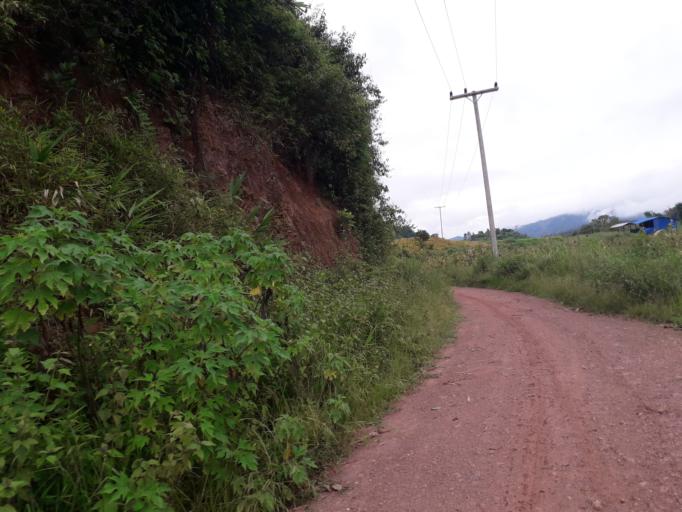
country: CN
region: Yunnan
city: Menglie
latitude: 22.2499
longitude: 101.6054
